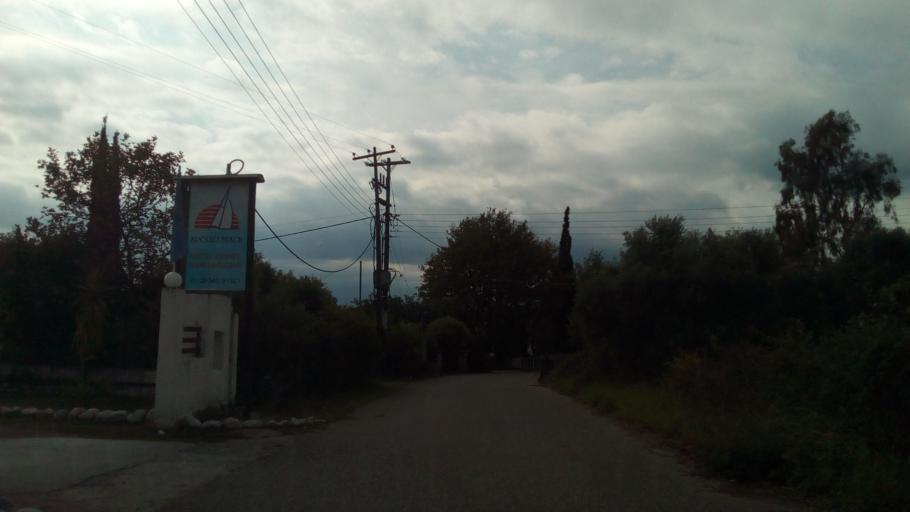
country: GR
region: West Greece
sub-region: Nomos Achaias
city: Kamarai
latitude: 38.3924
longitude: 22.0013
